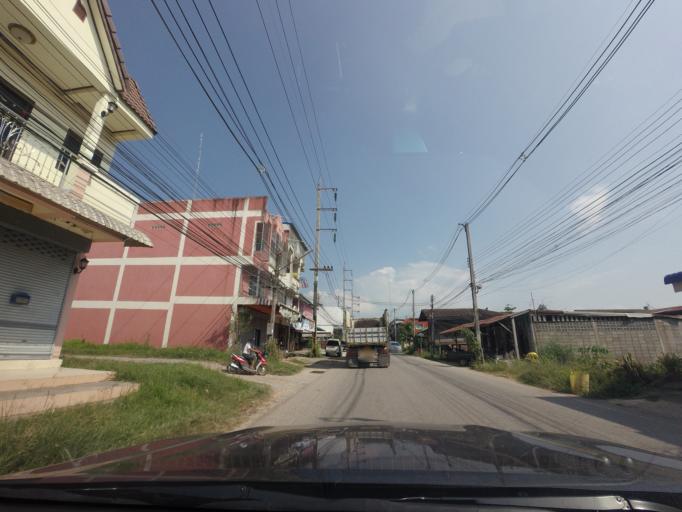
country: TH
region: Phitsanulok
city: Nakhon Thai
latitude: 17.1019
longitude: 100.8363
